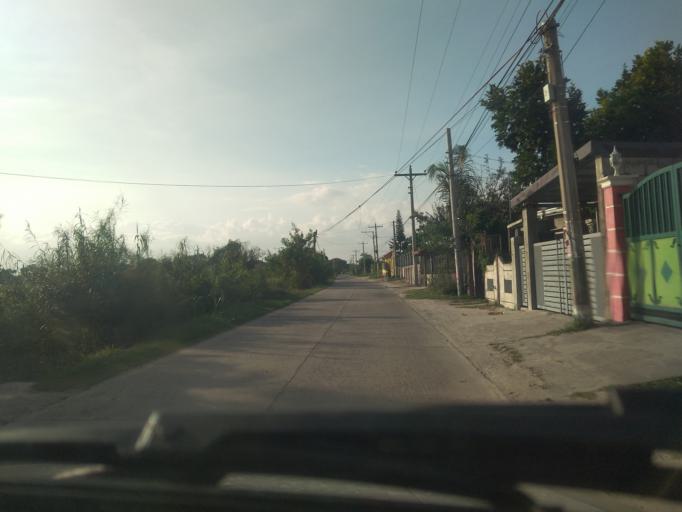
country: PH
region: Central Luzon
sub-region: Province of Pampanga
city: Mexico
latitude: 15.0821
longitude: 120.7017
